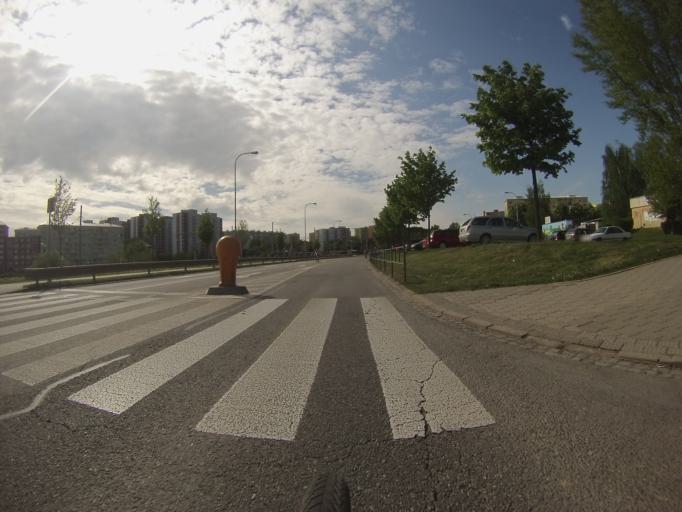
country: CZ
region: South Moravian
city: Troubsko
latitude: 49.2177
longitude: 16.5110
